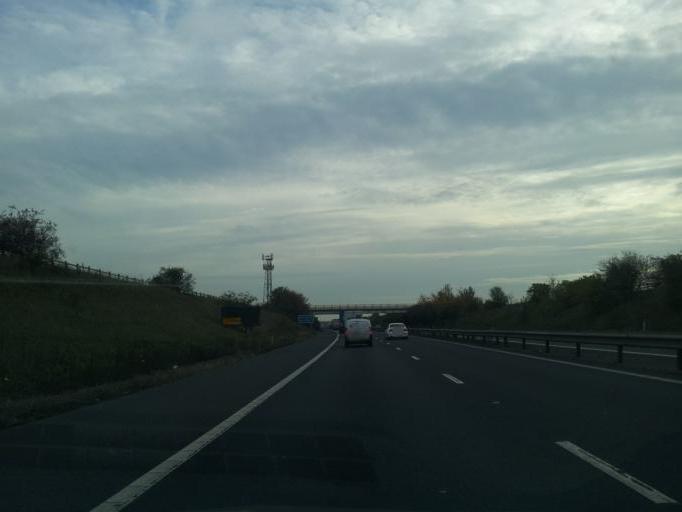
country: GB
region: England
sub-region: Cambridgeshire
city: Duxford
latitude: 52.1073
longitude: 0.1305
